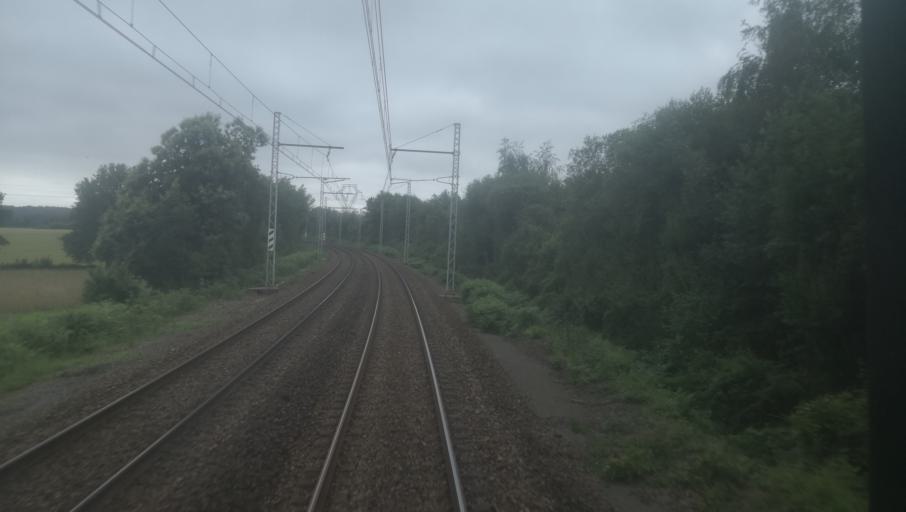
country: FR
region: Centre
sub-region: Departement de l'Indre
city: Chantome
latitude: 46.4086
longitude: 1.5472
